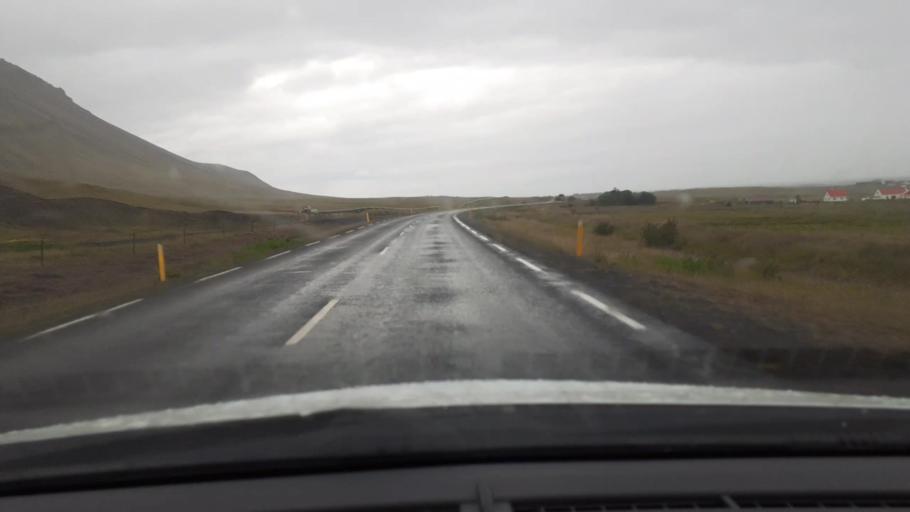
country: IS
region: West
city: Borgarnes
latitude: 64.3658
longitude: -21.8968
